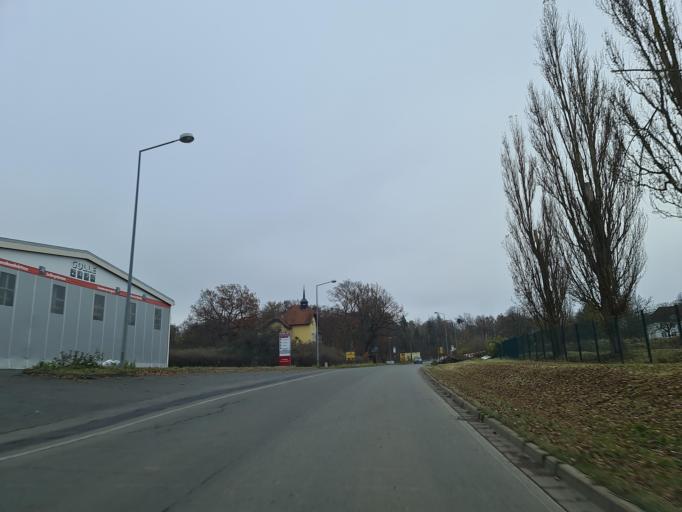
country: DE
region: Saxony
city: Plauen
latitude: 50.5030
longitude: 12.1006
